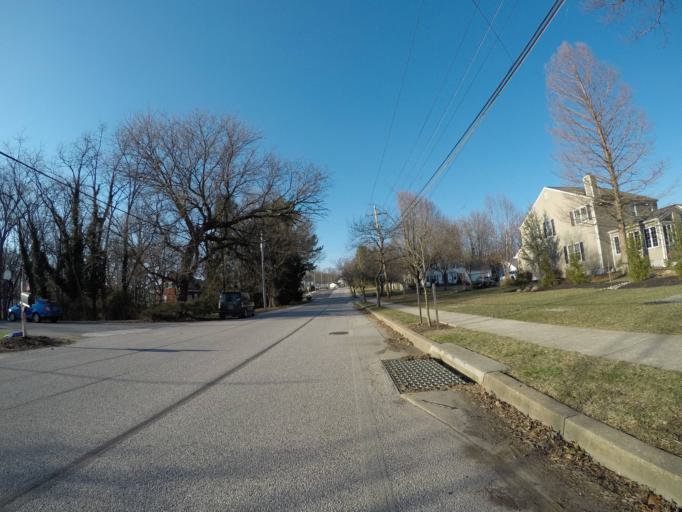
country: US
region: Maryland
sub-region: Howard County
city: Ilchester
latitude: 39.2518
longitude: -76.7447
